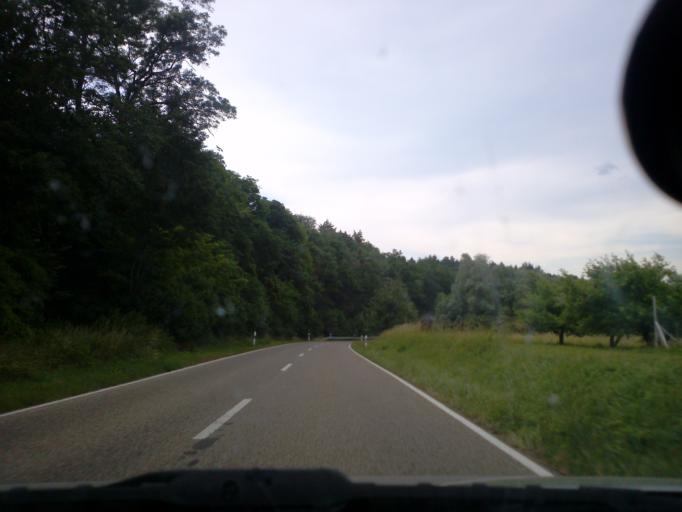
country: DE
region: Baden-Wuerttemberg
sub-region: Regierungsbezirk Stuttgart
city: Brackenheim
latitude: 49.0836
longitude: 9.0324
